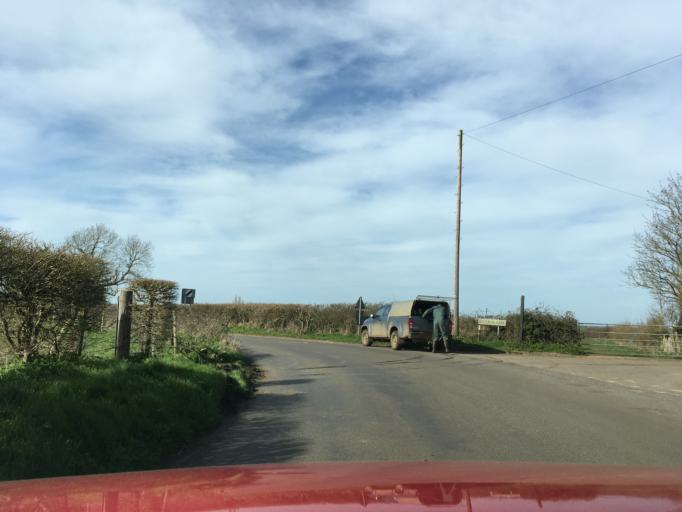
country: GB
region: England
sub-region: Wiltshire
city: Norton
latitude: 51.5189
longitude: -2.1378
